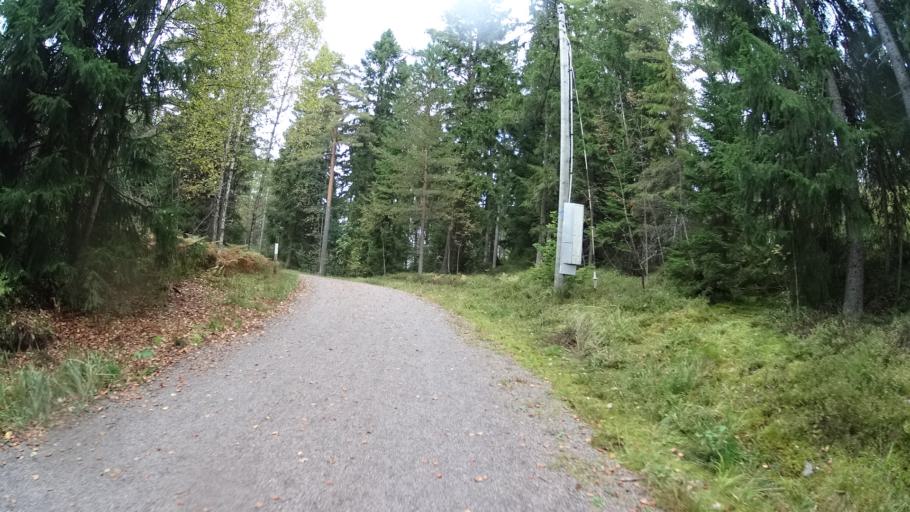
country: FI
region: Uusimaa
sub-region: Helsinki
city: Kauniainen
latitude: 60.1929
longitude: 24.7074
